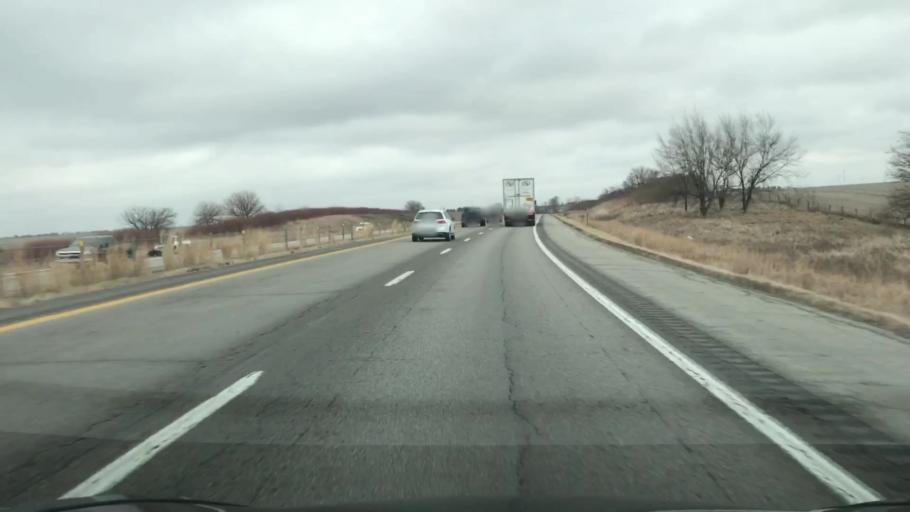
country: US
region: Iowa
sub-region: Guthrie County
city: Stuart
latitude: 41.4954
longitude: -94.3672
